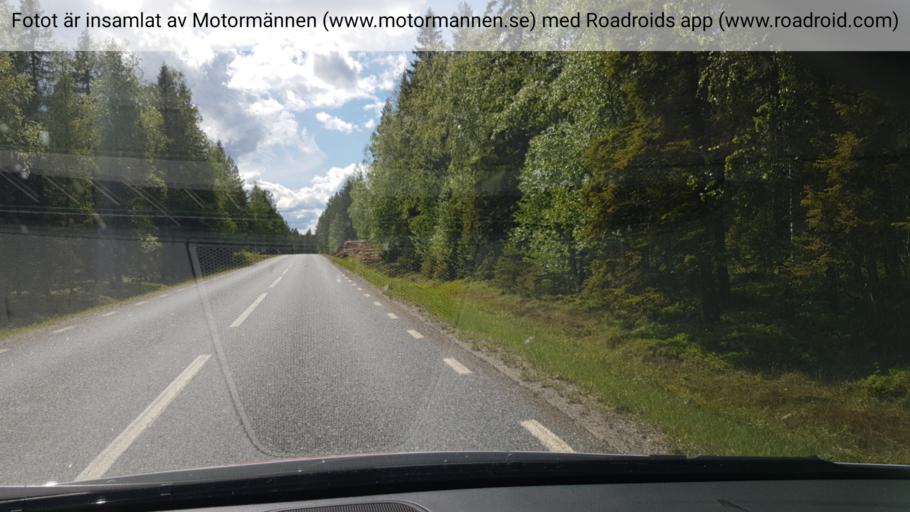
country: SE
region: Vaesterbotten
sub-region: Skelleftea Kommun
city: Burtraesk
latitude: 64.3974
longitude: 20.3219
